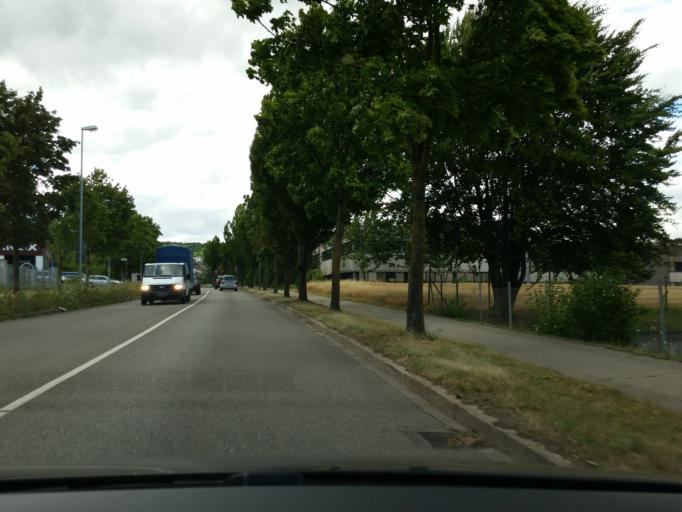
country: DE
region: Baden-Wuerttemberg
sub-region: Regierungsbezirk Stuttgart
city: Nurtingen
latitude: 48.6368
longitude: 9.3377
